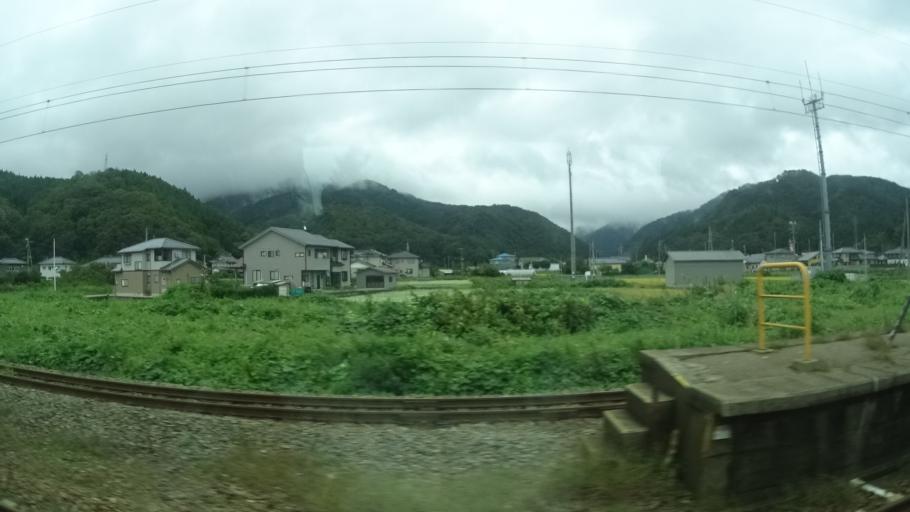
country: JP
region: Yamagata
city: Tsuruoka
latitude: 38.5565
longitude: 139.5488
